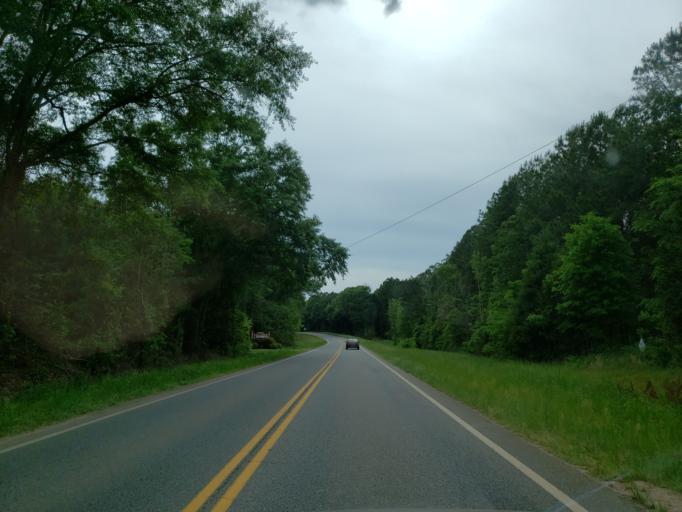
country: US
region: Georgia
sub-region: Macon County
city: Marshallville
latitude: 32.4150
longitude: -83.8605
